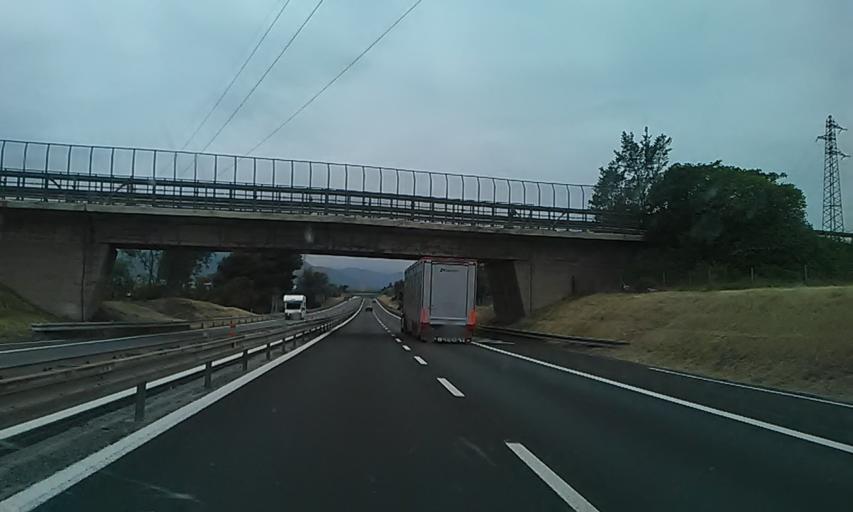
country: IT
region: Liguria
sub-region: Provincia di Savona
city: Campochiesa
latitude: 44.0748
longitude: 8.1868
